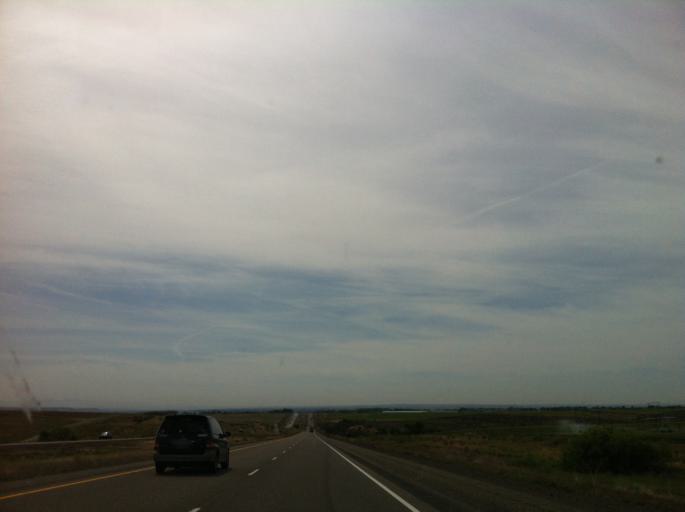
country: US
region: Oregon
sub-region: Malheur County
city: Ontario
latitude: 44.1059
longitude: -117.0484
